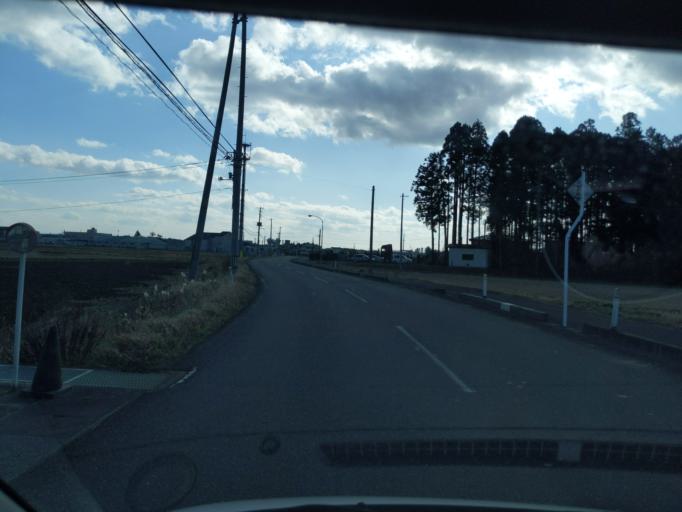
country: JP
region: Iwate
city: Ichinoseki
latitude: 38.7577
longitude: 141.0624
